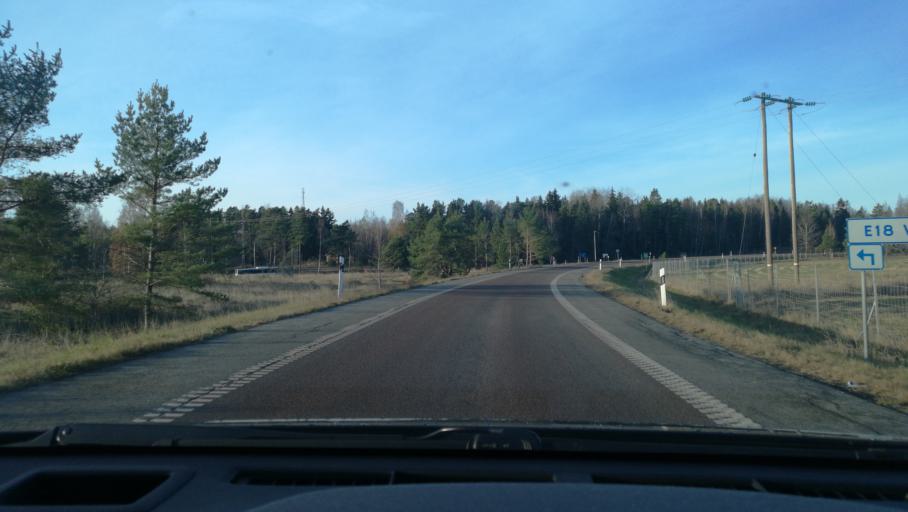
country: SE
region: Vaestmanland
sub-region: Hallstahammars Kommun
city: Kolback
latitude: 59.5927
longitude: 16.2509
